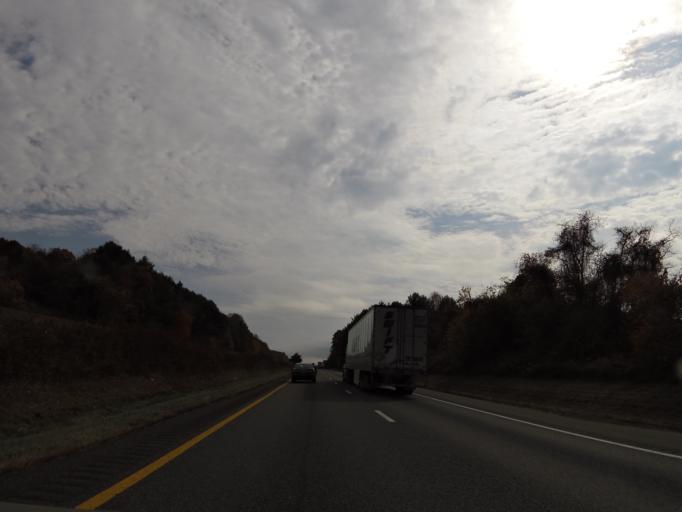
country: US
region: Virginia
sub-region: Carroll County
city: Hillsville
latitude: 36.7153
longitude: -80.7448
